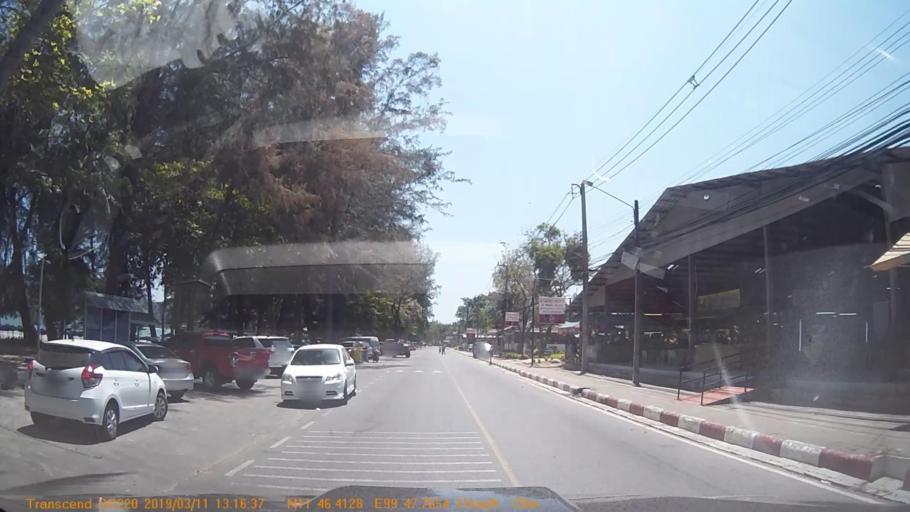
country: TH
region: Prachuap Khiri Khan
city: Prachuap Khiri Khan
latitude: 11.7735
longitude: 99.7961
